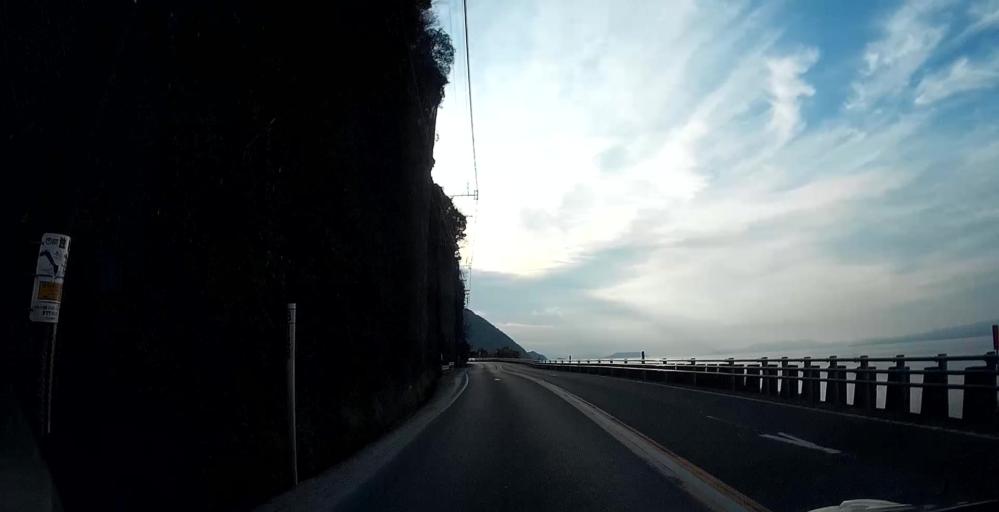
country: JP
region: Nagasaki
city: Shimabara
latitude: 32.6345
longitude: 130.4626
